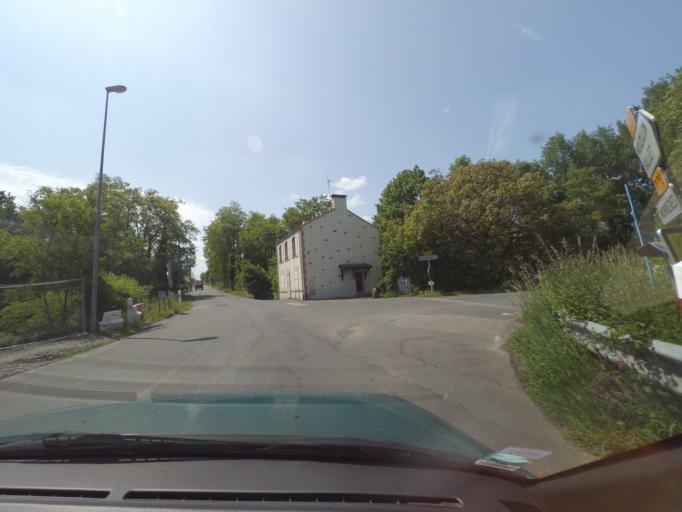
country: FR
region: Pays de la Loire
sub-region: Departement de la Loire-Atlantique
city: Gorges
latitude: 47.1057
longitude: -1.3048
